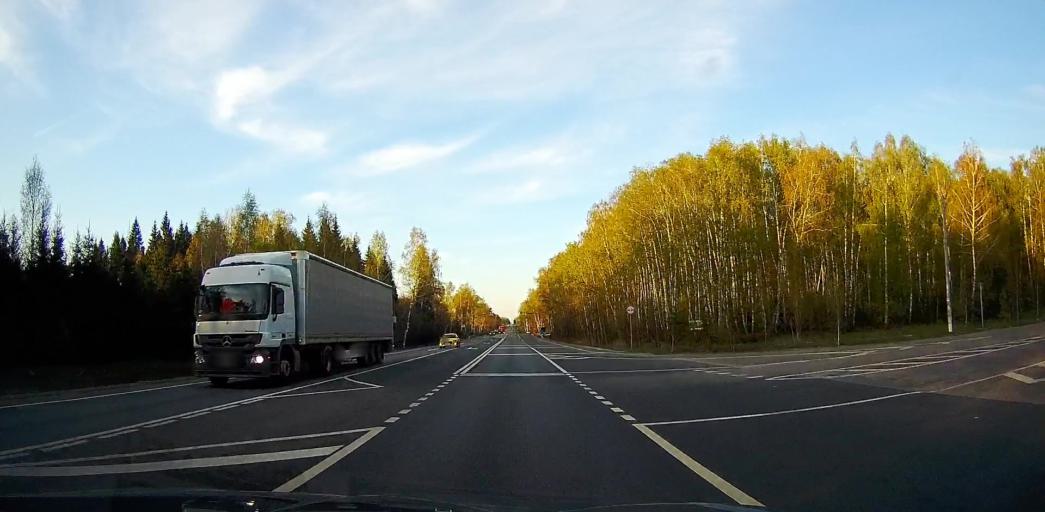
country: RU
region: Moskovskaya
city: Meshcherino
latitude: 55.2345
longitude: 38.4188
